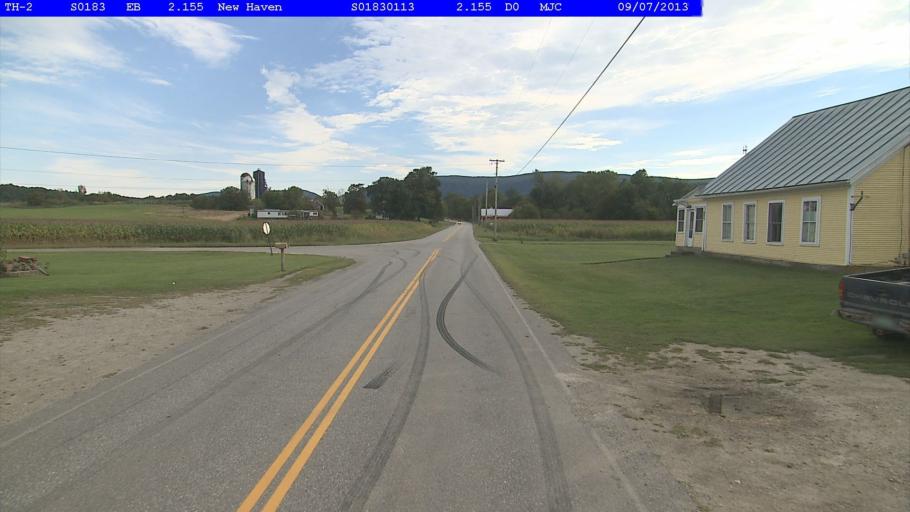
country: US
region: Vermont
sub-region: Addison County
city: Middlebury (village)
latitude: 44.0722
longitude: -73.1346
